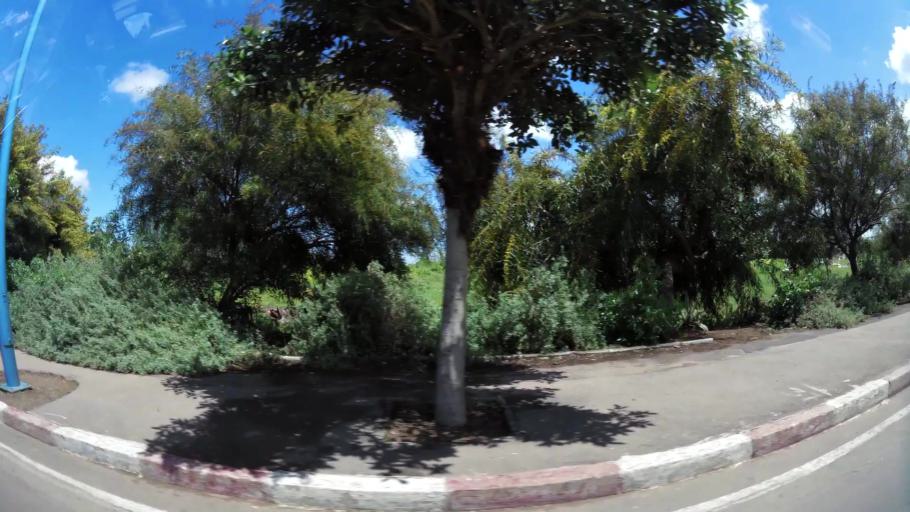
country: MA
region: Grand Casablanca
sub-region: Casablanca
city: Casablanca
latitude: 33.5210
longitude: -7.6317
